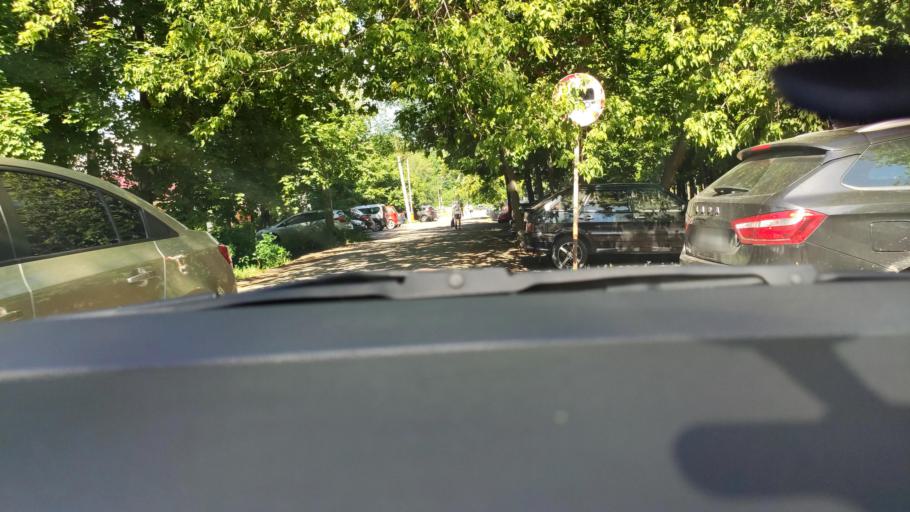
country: RU
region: Voronezj
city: Ramon'
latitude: 51.9138
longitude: 39.3094
